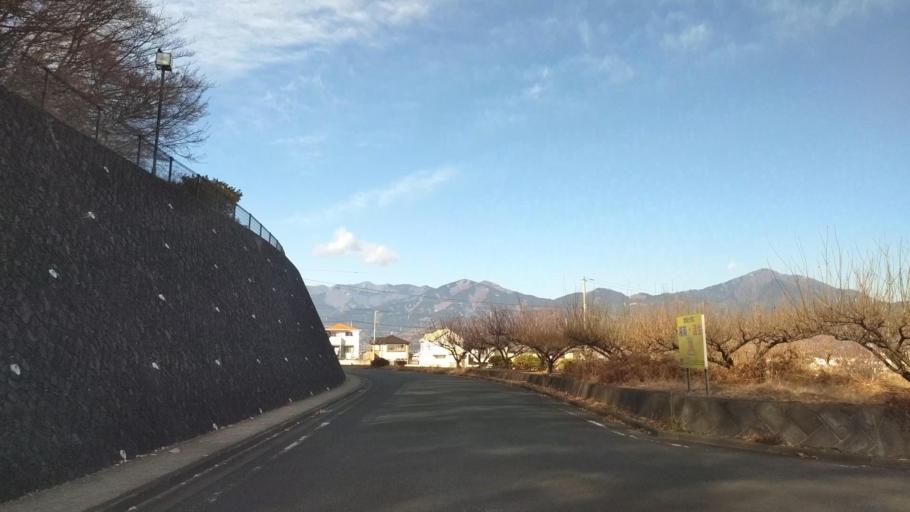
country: JP
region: Kanagawa
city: Hadano
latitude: 35.3586
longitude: 139.2272
